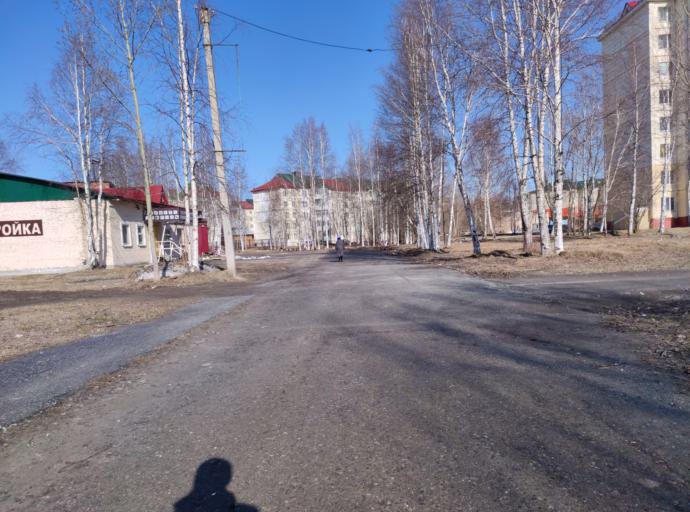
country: RU
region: Khanty-Mansiyskiy Avtonomnyy Okrug
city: Langepas
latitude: 61.2511
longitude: 75.1724
